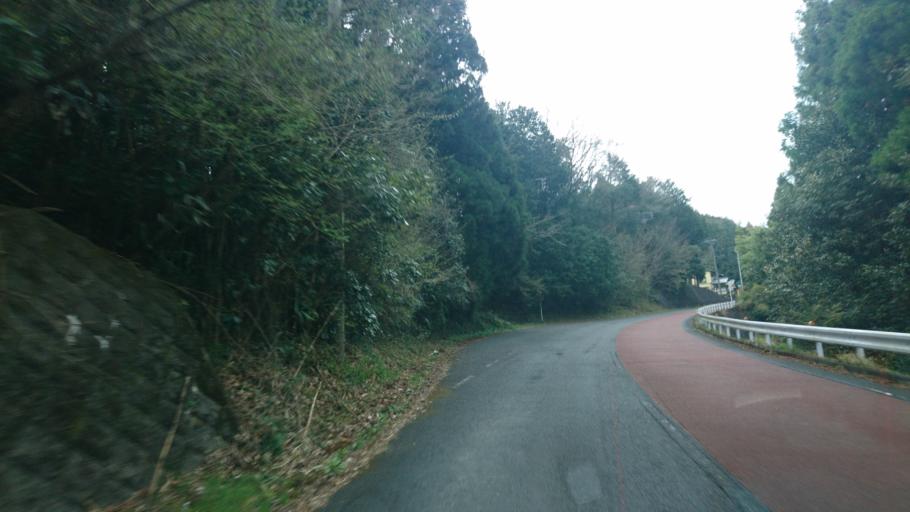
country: JP
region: Shizuoka
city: Fujinomiya
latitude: 35.2971
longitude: 138.5785
